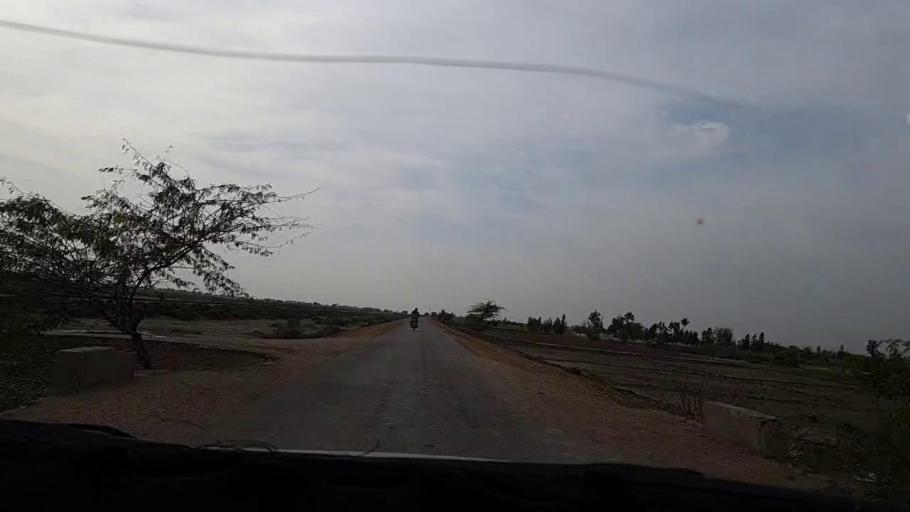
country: PK
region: Sindh
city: Pithoro
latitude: 25.5165
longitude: 69.2716
